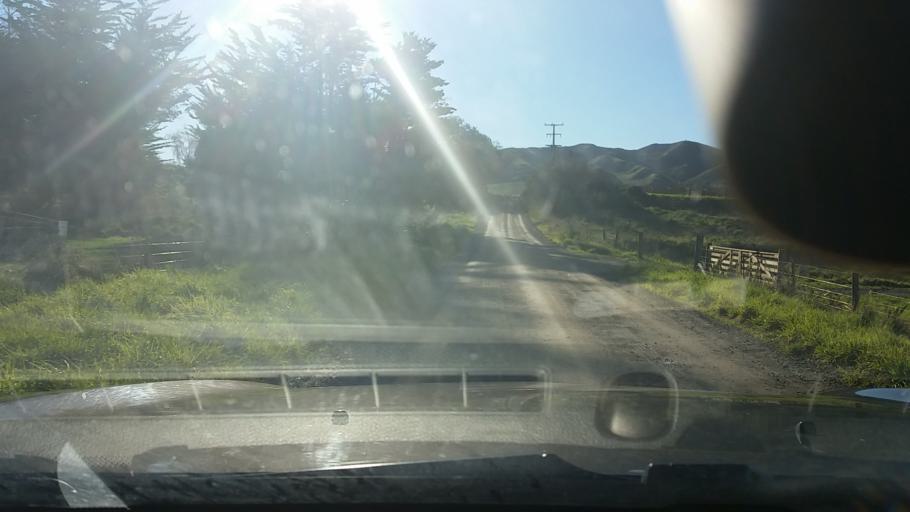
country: NZ
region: Marlborough
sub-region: Marlborough District
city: Blenheim
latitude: -41.6485
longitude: 174.0550
